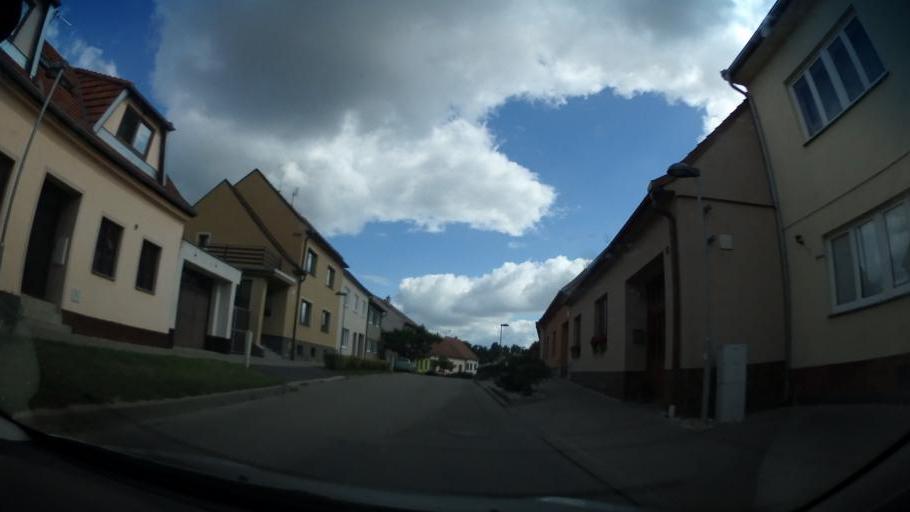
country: CZ
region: South Moravian
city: Orechov
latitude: 49.1127
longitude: 16.5173
